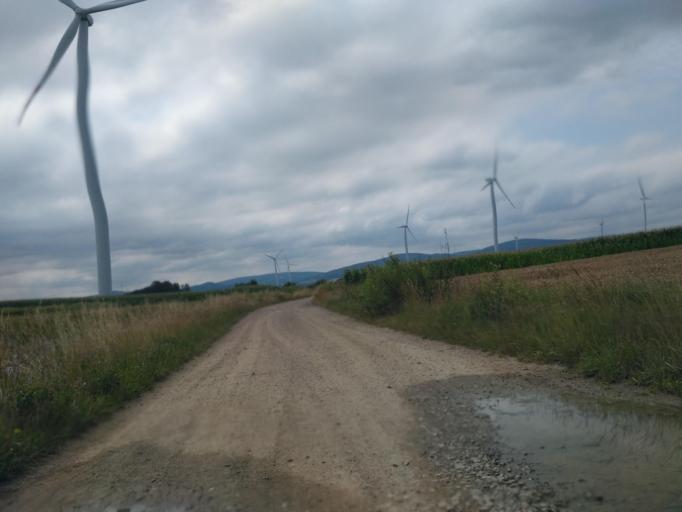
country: PL
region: Subcarpathian Voivodeship
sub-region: Powiat krosnienski
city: Rymanow
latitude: 49.6166
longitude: 21.8472
